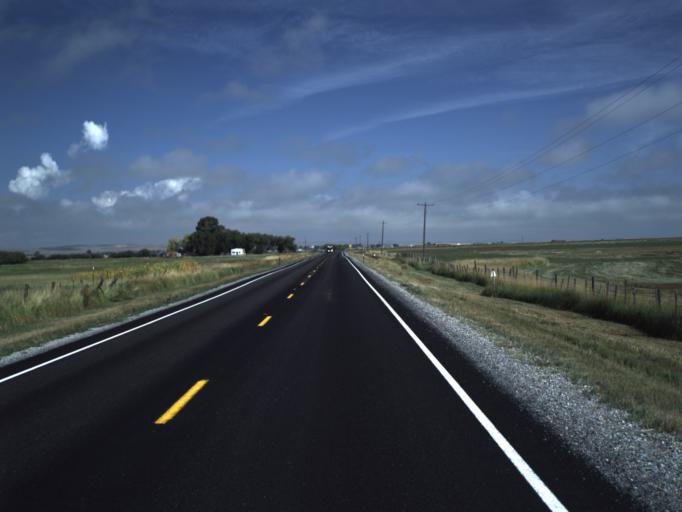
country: US
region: Utah
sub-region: Rich County
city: Randolph
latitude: 41.6302
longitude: -111.1790
